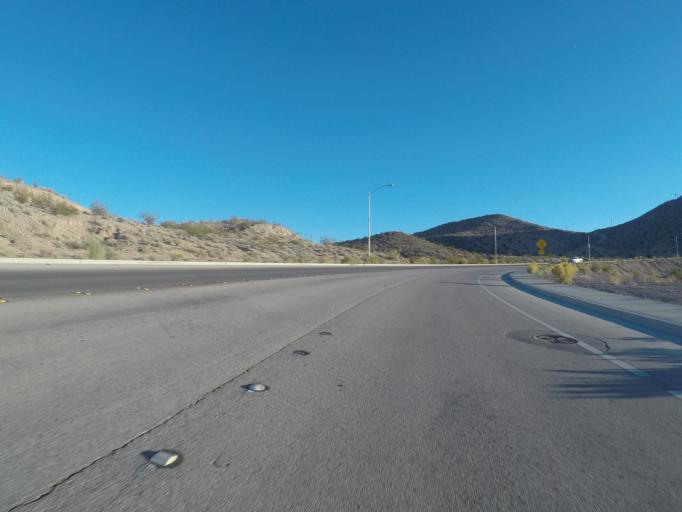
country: US
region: Nevada
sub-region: Clark County
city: Boulder City
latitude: 35.9837
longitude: -114.8279
